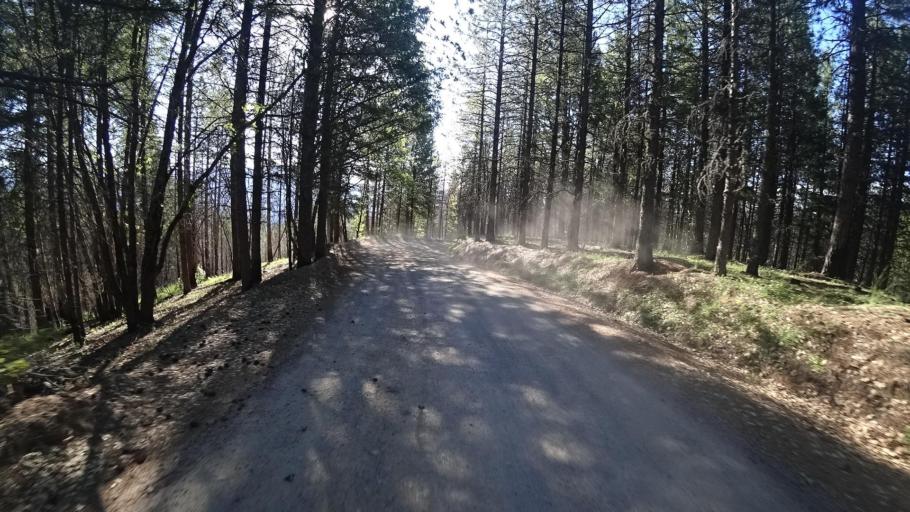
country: US
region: California
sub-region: Lake County
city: Upper Lake
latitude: 39.3498
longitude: -122.9709
